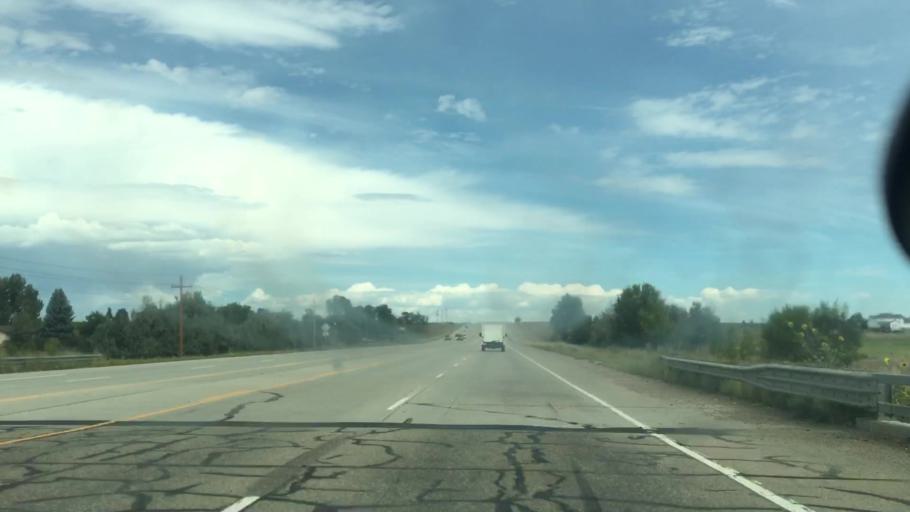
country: US
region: Colorado
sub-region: Larimer County
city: Berthoud
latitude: 40.2776
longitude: -105.1024
